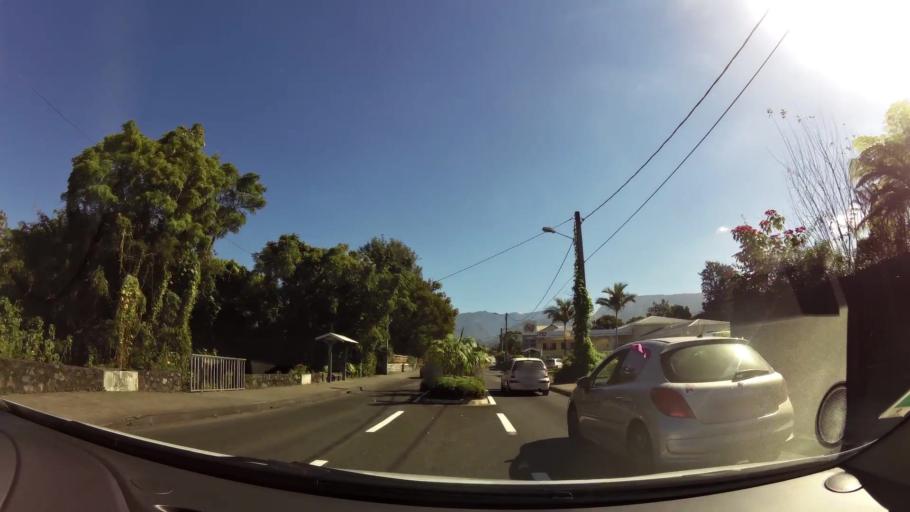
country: RE
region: Reunion
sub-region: Reunion
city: Le Tampon
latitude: -21.2659
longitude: 55.5086
